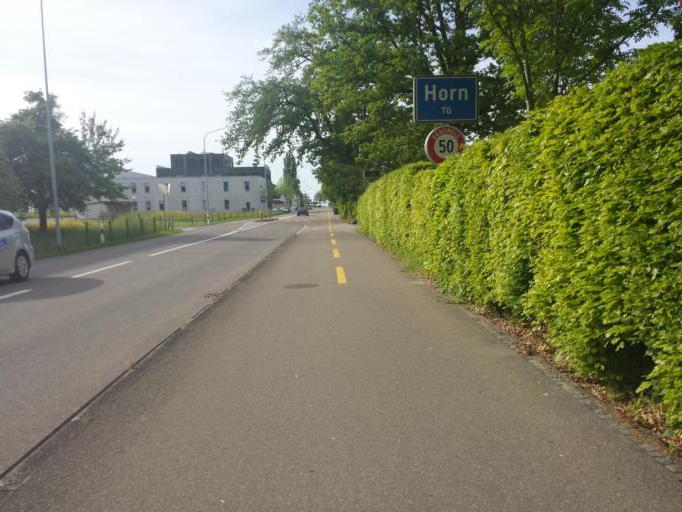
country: CH
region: Saint Gallen
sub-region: Wahlkreis Rorschach
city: Horn
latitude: 47.4900
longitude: 9.4727
